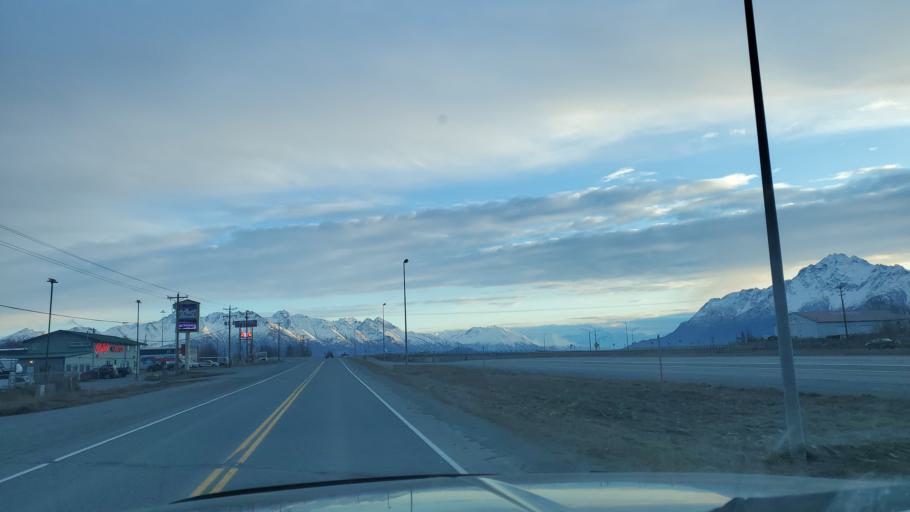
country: US
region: Alaska
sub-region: Matanuska-Susitna Borough
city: Gateway
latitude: 61.5633
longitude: -149.2741
